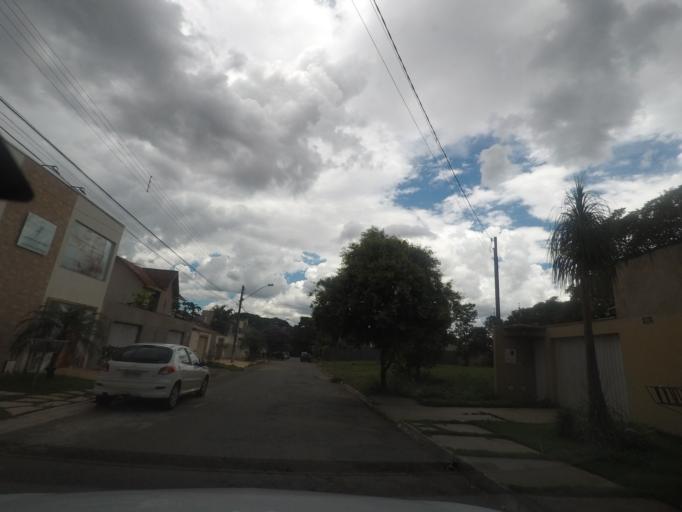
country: BR
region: Goias
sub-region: Goiania
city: Goiania
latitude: -16.6410
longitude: -49.2244
